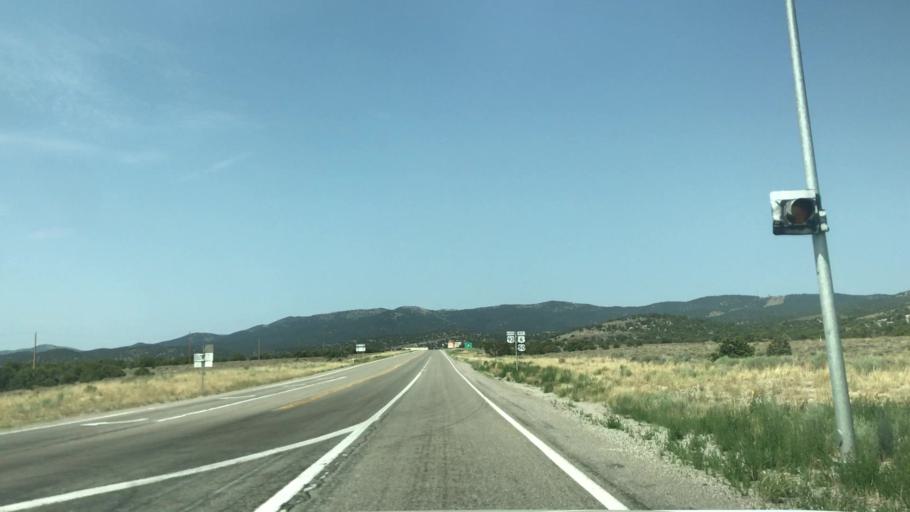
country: US
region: Nevada
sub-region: White Pine County
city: Ely
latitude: 39.0277
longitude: -114.5742
